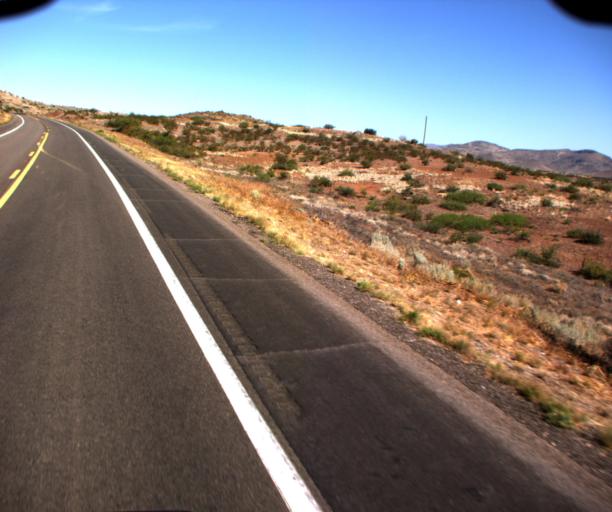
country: US
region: Arizona
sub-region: Greenlee County
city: Clifton
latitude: 32.7486
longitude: -109.2294
